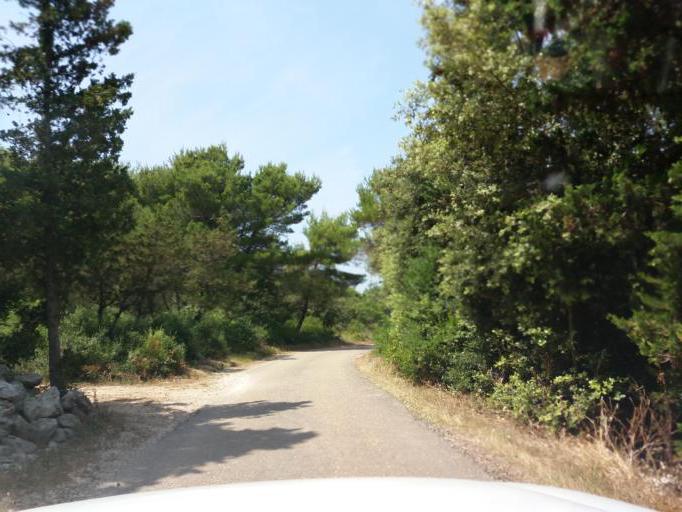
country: HR
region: Zadarska
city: Ugljan
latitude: 44.1414
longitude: 14.8465
